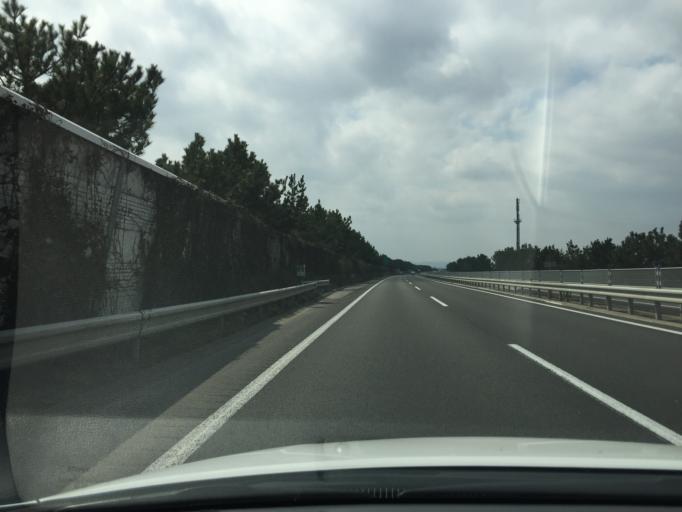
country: JP
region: Miyagi
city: Iwanuma
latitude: 38.1752
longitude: 140.9252
